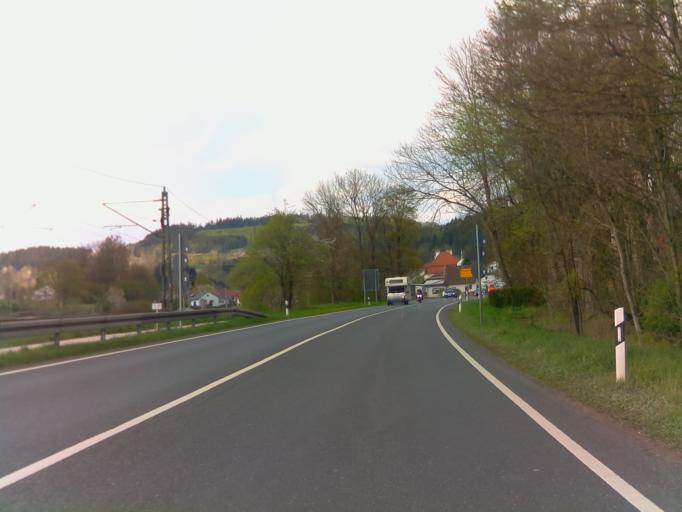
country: DE
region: Bavaria
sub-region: Upper Franconia
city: Pressig
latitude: 50.3567
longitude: 11.3183
